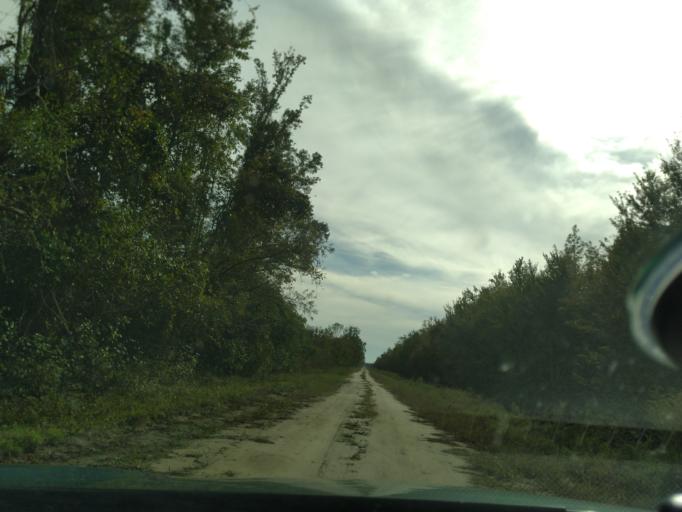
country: US
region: North Carolina
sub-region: Beaufort County
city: Belhaven
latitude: 35.7258
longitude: -76.5723
